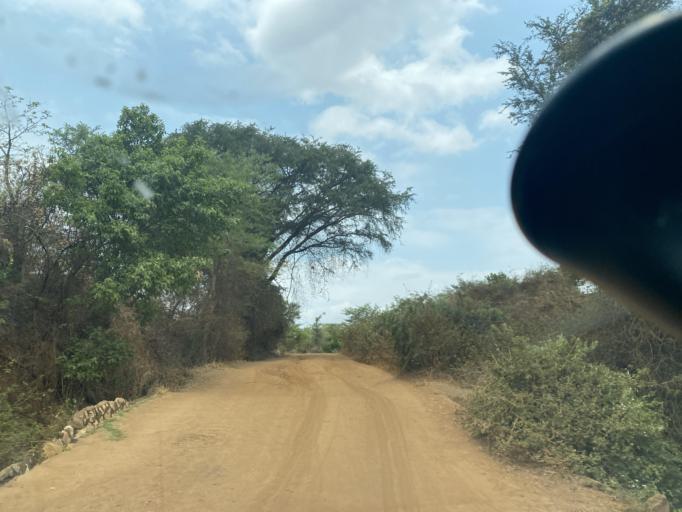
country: ZM
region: Lusaka
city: Chongwe
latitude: -15.5102
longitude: 28.8181
